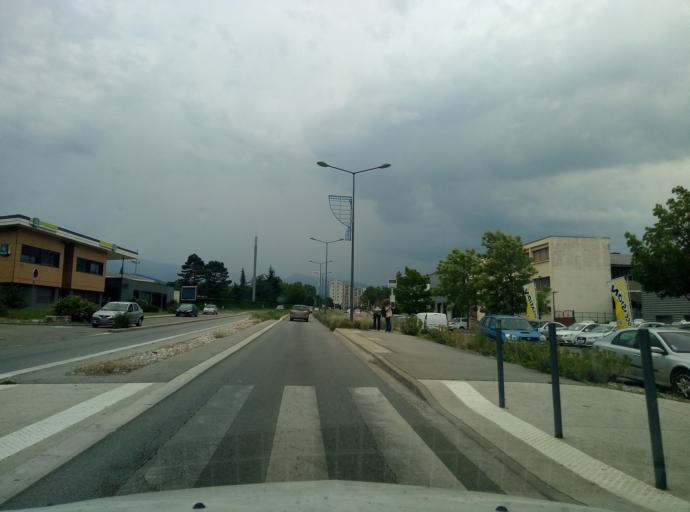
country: FR
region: Rhone-Alpes
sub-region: Departement de l'Isere
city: Seyssinet-Pariset
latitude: 45.1867
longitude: 5.6870
